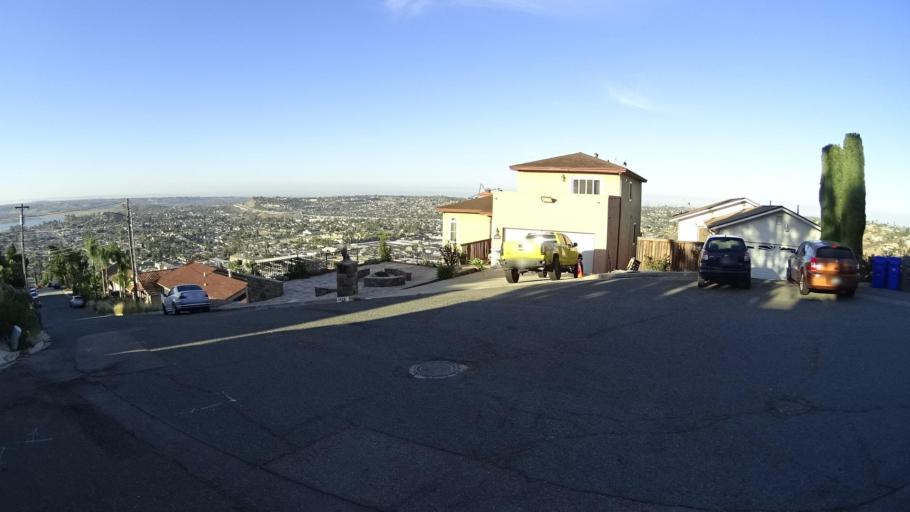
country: US
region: California
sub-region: San Diego County
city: La Presa
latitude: 32.7195
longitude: -116.9962
